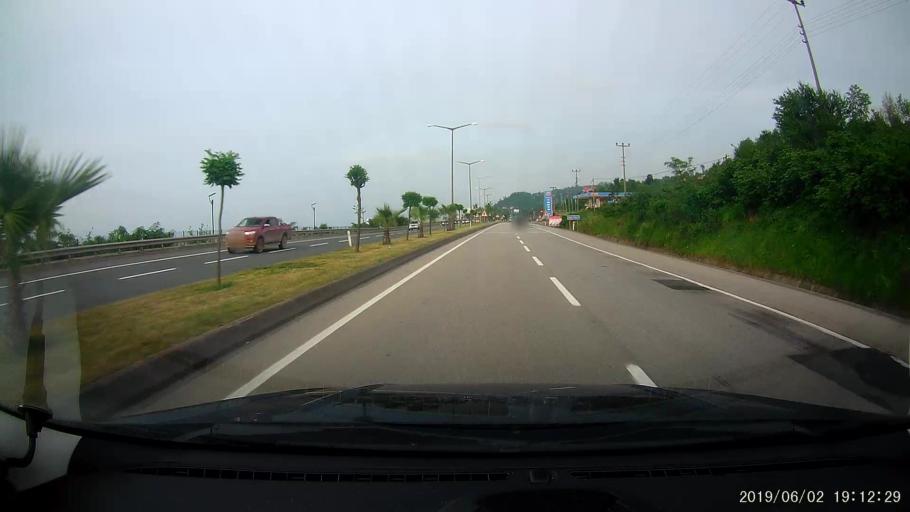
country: TR
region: Ordu
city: Gulyali
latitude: 40.9653
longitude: 38.0702
